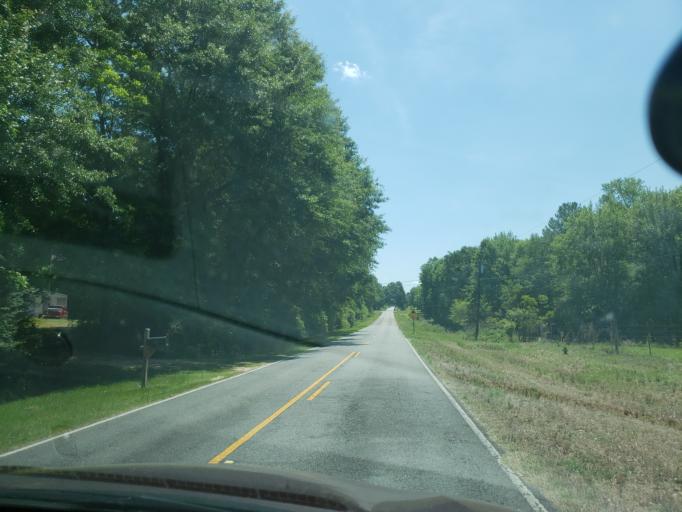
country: US
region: Alabama
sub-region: Elmore County
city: Tallassee
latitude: 32.5810
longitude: -85.8019
